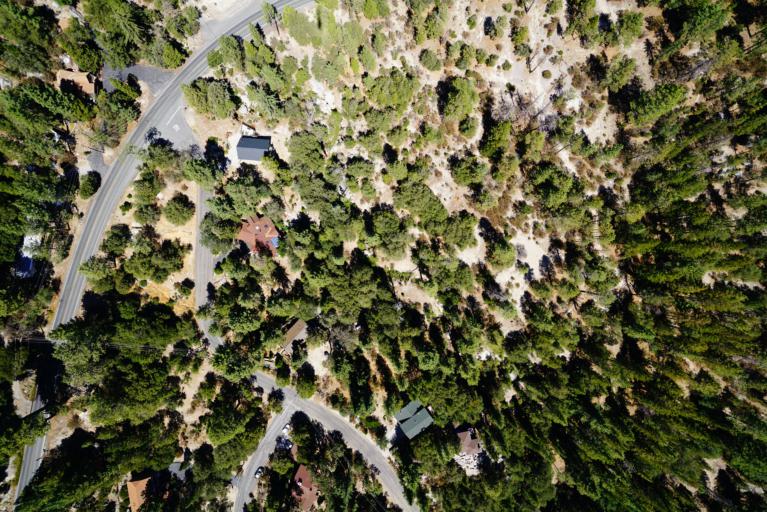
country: US
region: California
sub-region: Riverside County
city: Idyllwild-Pine Cove
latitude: 33.7524
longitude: -116.7243
